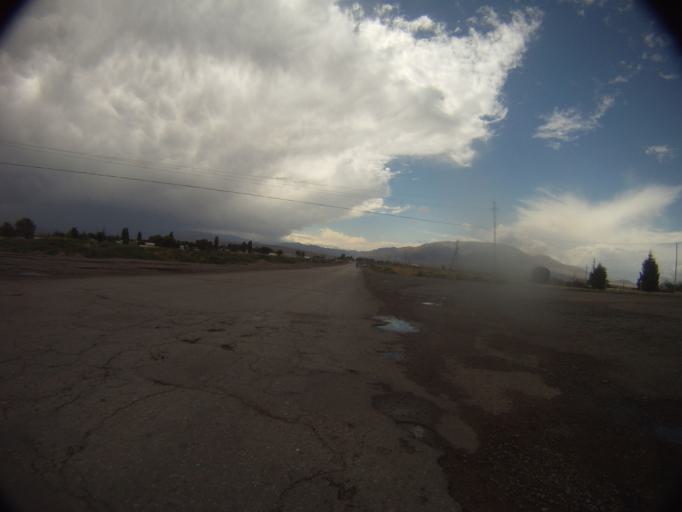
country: KG
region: Ysyk-Koel
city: Balykchy
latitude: 42.4498
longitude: 76.1572
